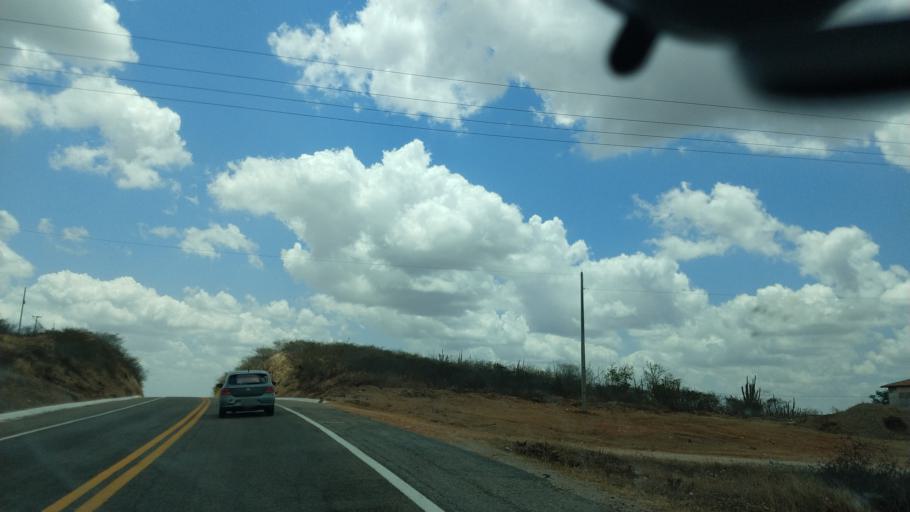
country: BR
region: Rio Grande do Norte
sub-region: Cerro Cora
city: Cerro Cora
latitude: -6.1878
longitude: -36.2371
